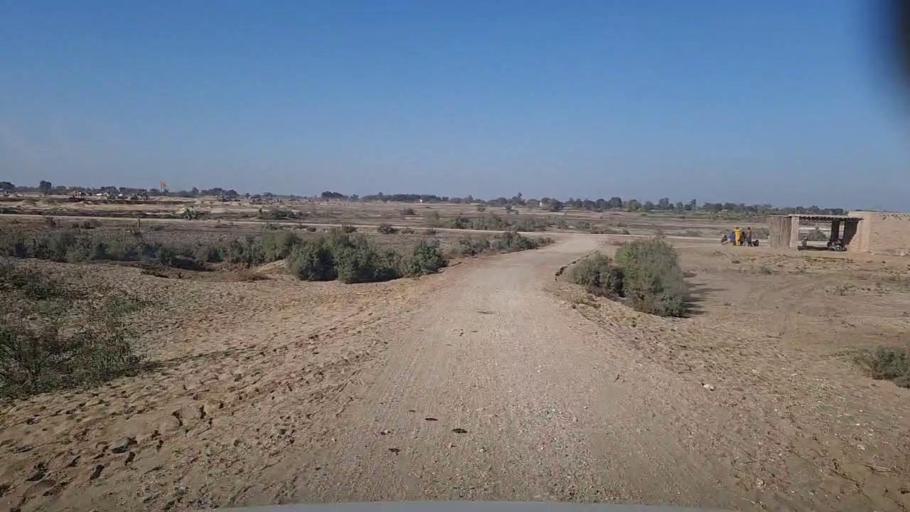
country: PK
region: Sindh
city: Khairpur
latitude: 27.9638
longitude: 69.8112
